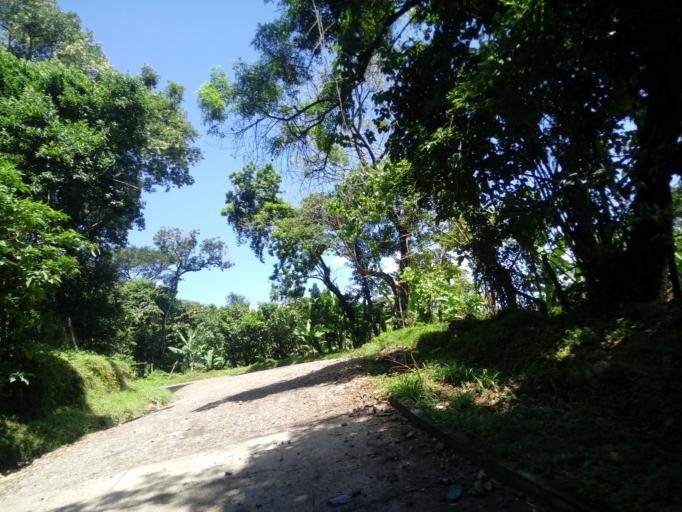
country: GT
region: Guatemala
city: Villa Canales
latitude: 14.4151
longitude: -90.5551
